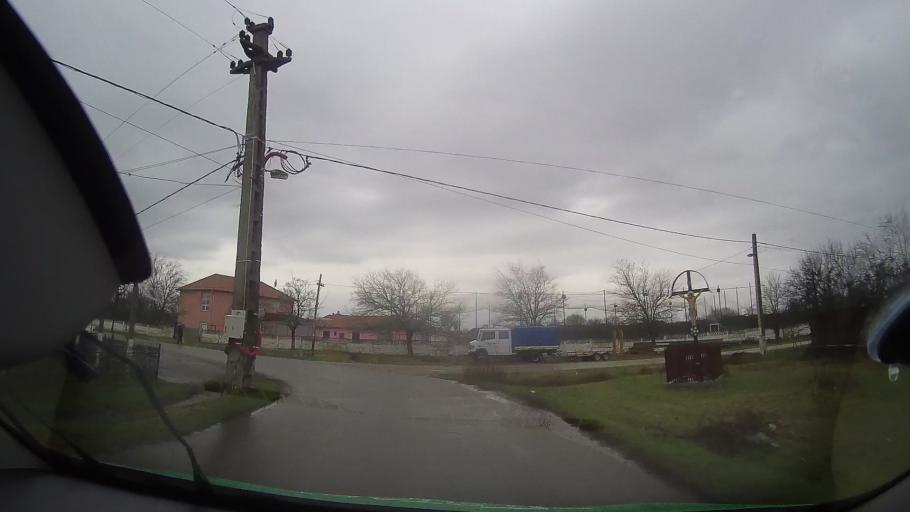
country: RO
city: Capalna
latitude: 46.7378
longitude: 22.1019
